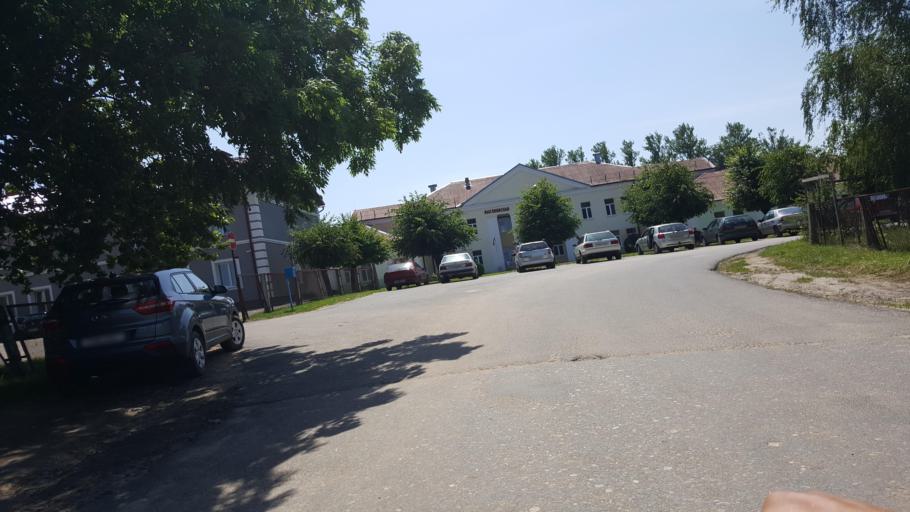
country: BY
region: Brest
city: Vysokaye
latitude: 52.3635
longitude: 23.3934
